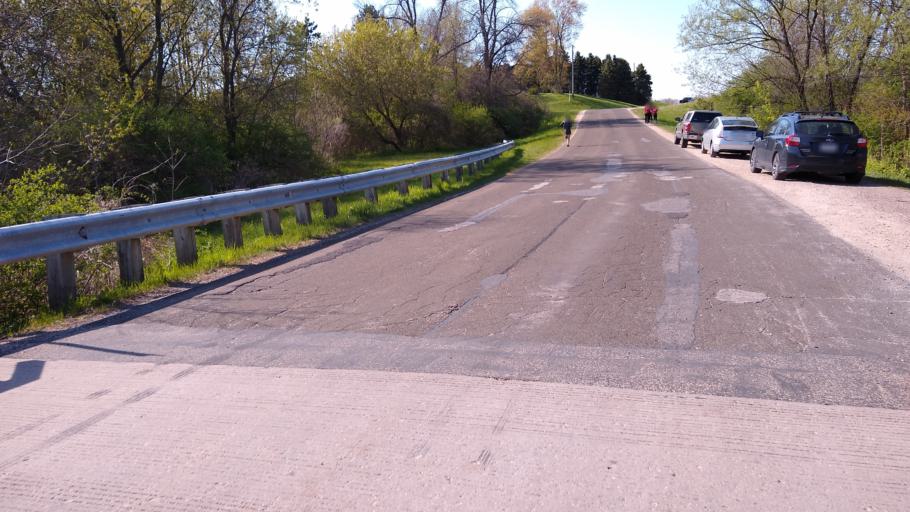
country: US
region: Wisconsin
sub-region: Dane County
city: Waunakee
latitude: 43.1409
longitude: -89.4377
